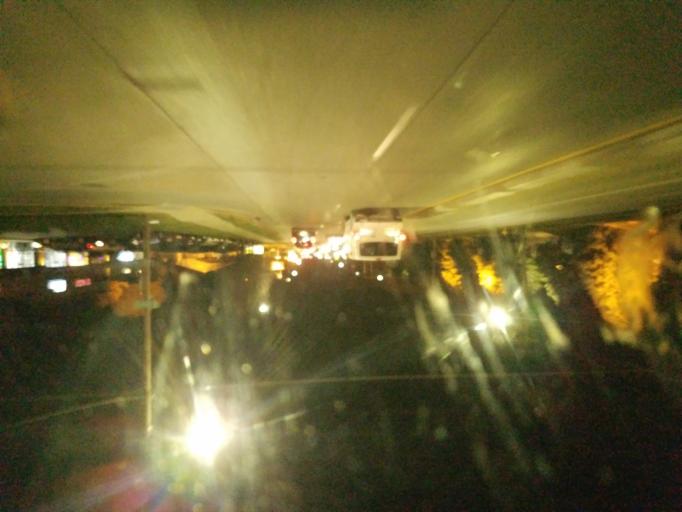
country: US
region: Iowa
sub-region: Polk County
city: Des Moines
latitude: 41.6004
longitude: -93.5742
